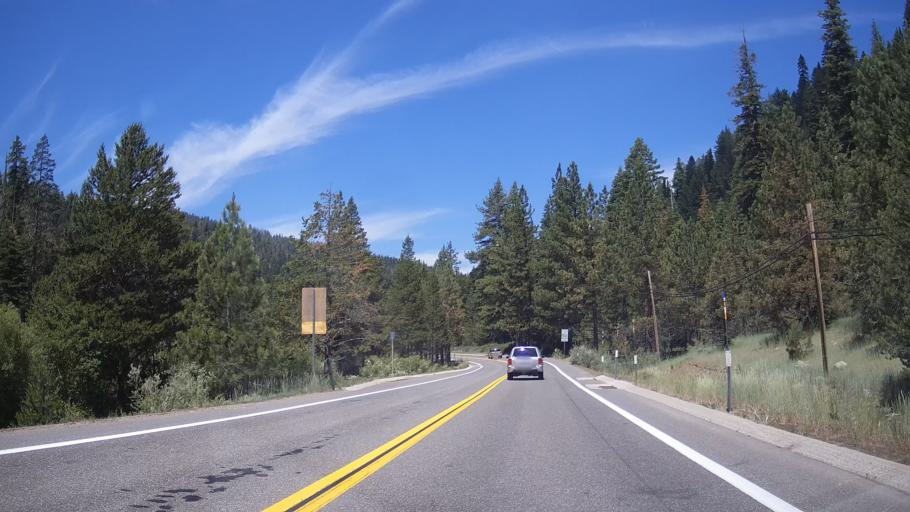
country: US
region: California
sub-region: Placer County
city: Sunnyside-Tahoe City
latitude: 39.1660
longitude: -120.1791
